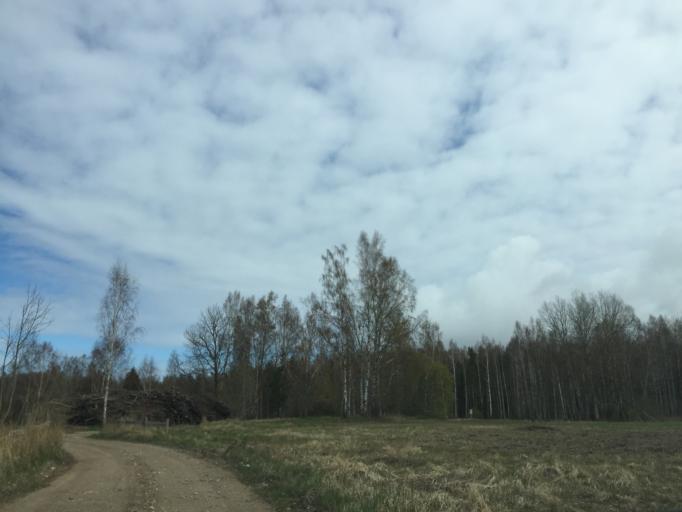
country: LV
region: Salacgrivas
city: Salacgriva
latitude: 57.5422
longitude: 24.3670
